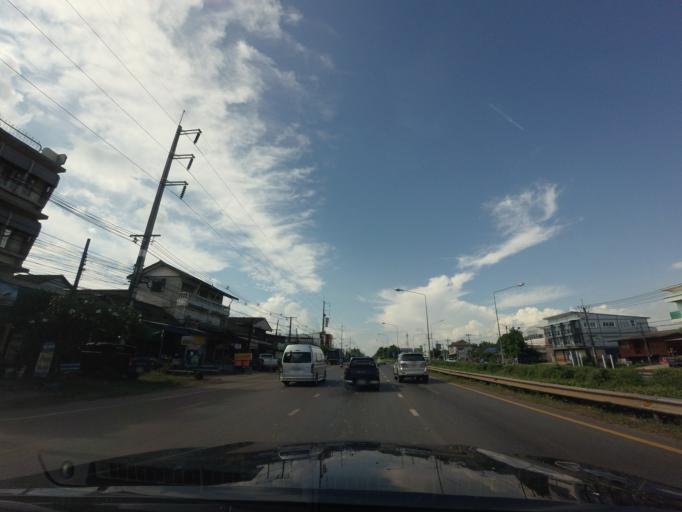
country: TH
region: Nong Khai
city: Sa Khrai
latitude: 17.7735
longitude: 102.7671
